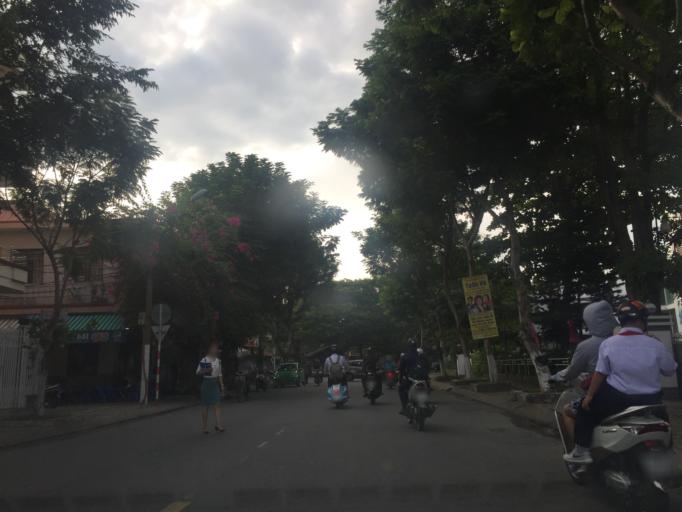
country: VN
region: Da Nang
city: Da Nang
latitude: 16.0802
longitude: 108.2111
